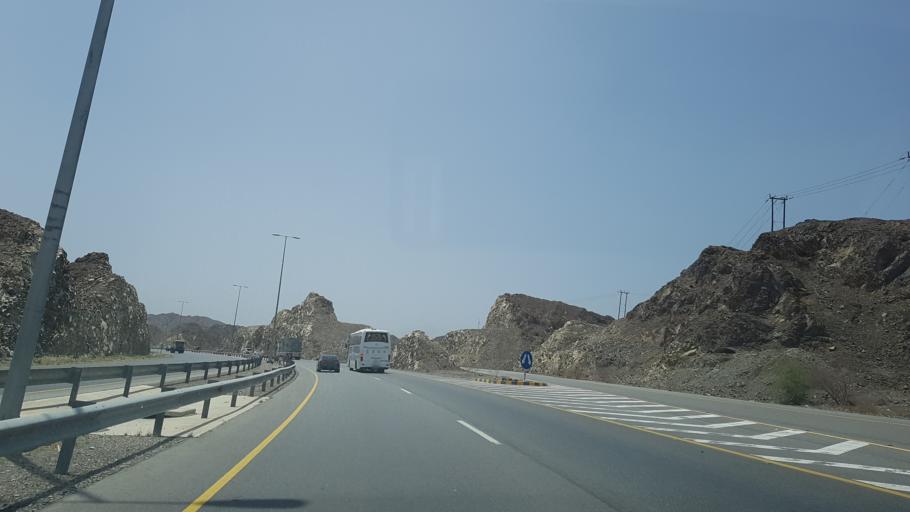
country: OM
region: Muhafazat ad Dakhiliyah
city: Sufalat Sama'il
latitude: 23.3632
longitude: 58.0336
